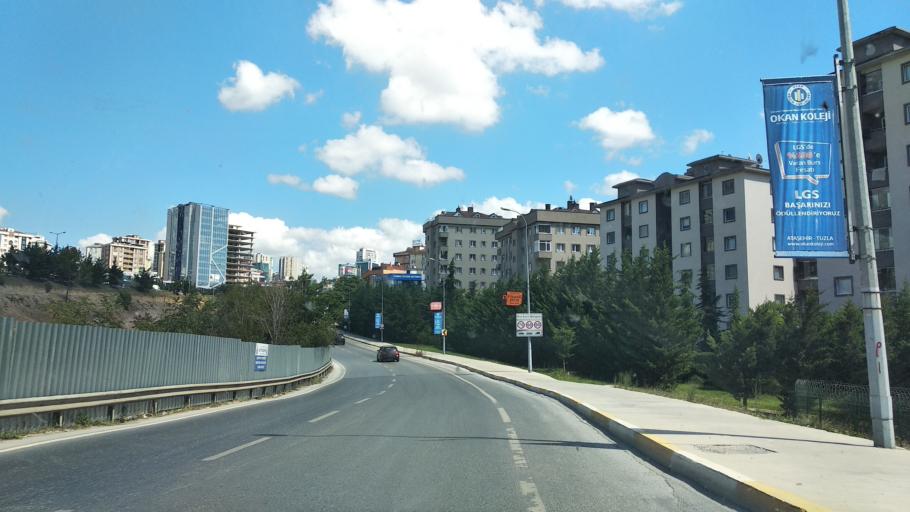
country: TR
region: Istanbul
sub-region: Atasehir
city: Atasehir
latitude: 40.9957
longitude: 29.1305
